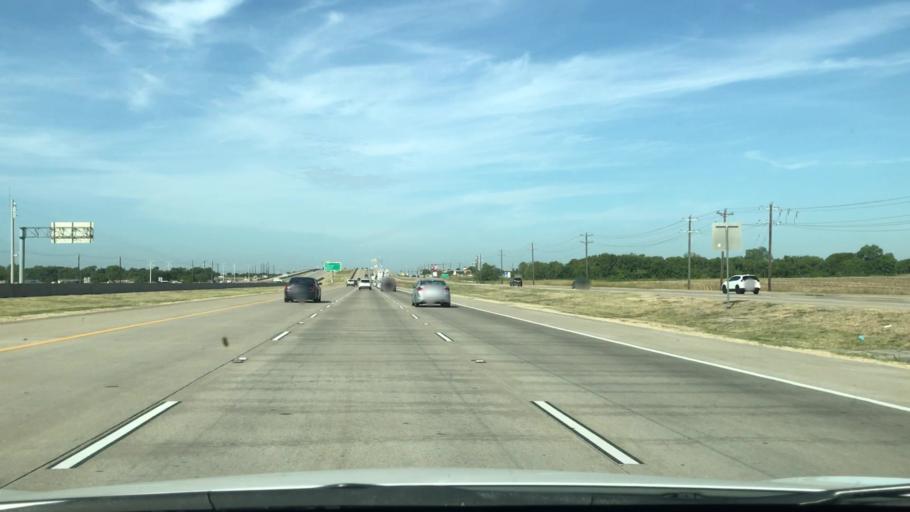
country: US
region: Texas
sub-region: Collin County
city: Allen
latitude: 33.1436
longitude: -96.6825
